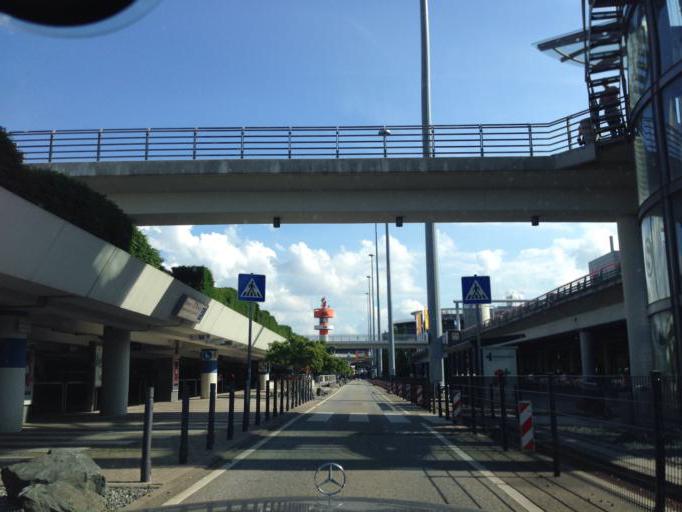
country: DE
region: Hamburg
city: Fuhlsbuettel
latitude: 53.6324
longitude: 10.0068
